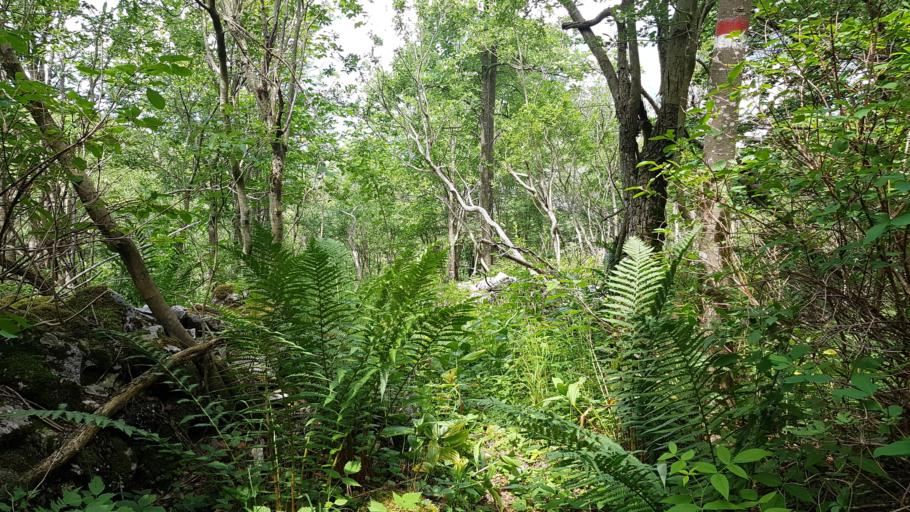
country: IT
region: Friuli Venezia Giulia
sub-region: Provincia di Udine
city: Lusevera
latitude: 46.2934
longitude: 13.3040
